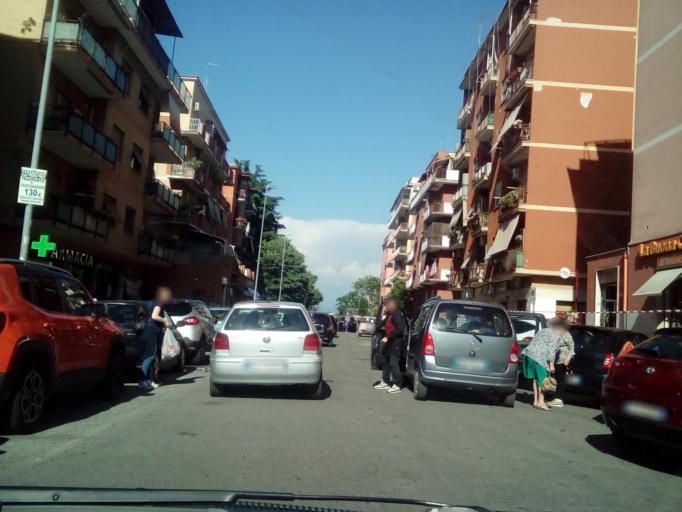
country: IT
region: Latium
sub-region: Citta metropolitana di Roma Capitale
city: Rome
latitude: 41.8881
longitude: 12.5675
